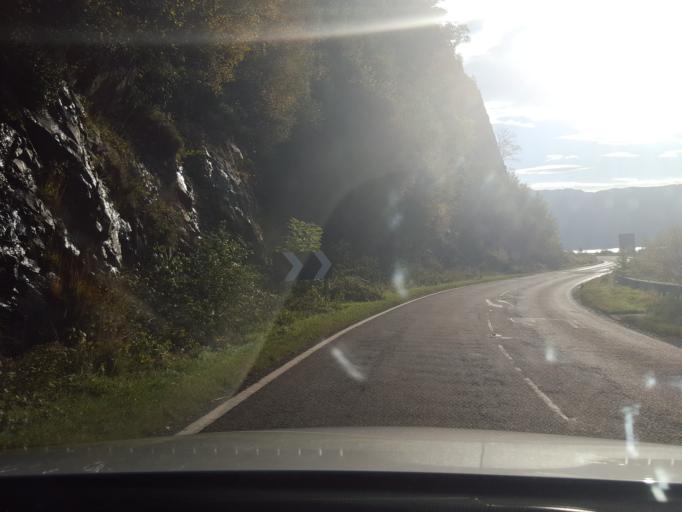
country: GB
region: Scotland
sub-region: Highland
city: Fort William
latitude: 57.2695
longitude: -5.5075
